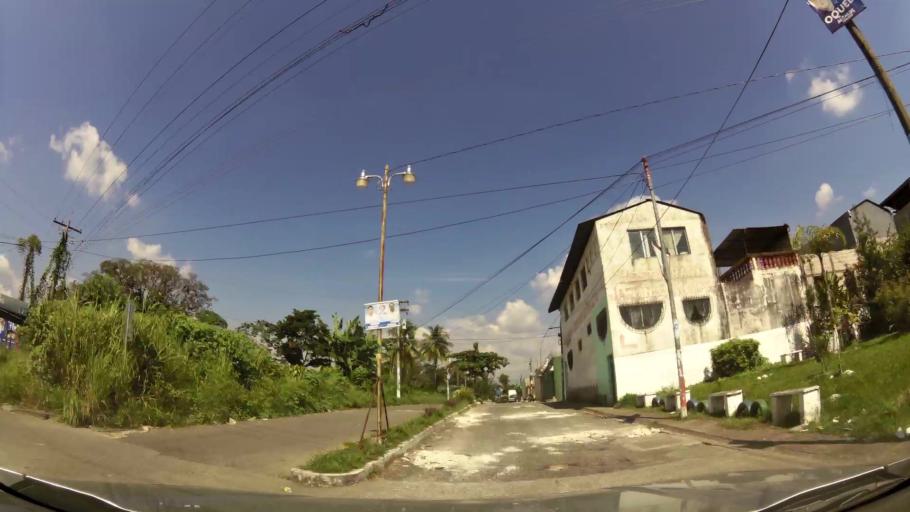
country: GT
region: Suchitepeque
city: Mazatenango
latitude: 14.5330
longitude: -91.4847
